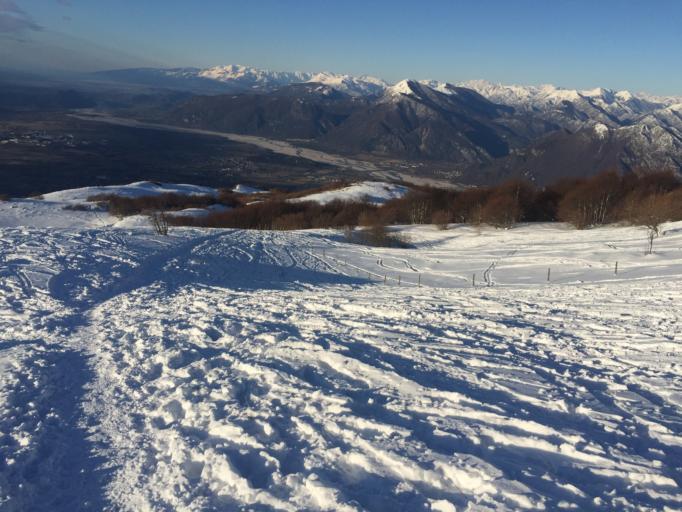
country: IT
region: Friuli Venezia Giulia
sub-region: Provincia di Udine
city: Isola
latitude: 46.2764
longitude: 13.1785
